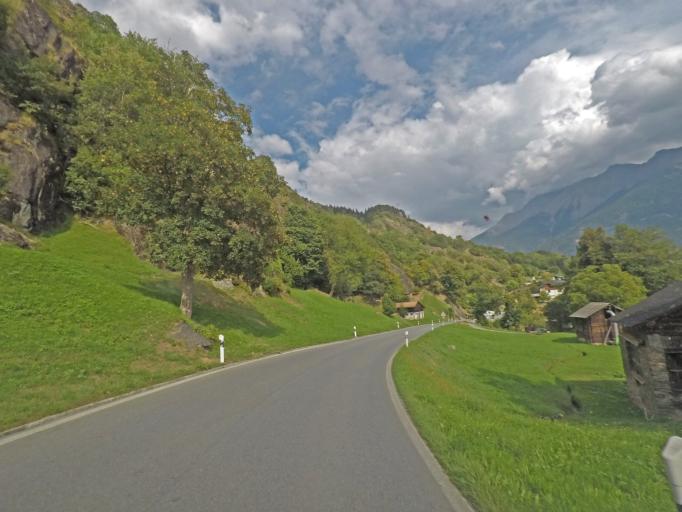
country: CH
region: Valais
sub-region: Brig District
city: Naters
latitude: 46.3349
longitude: 7.9877
